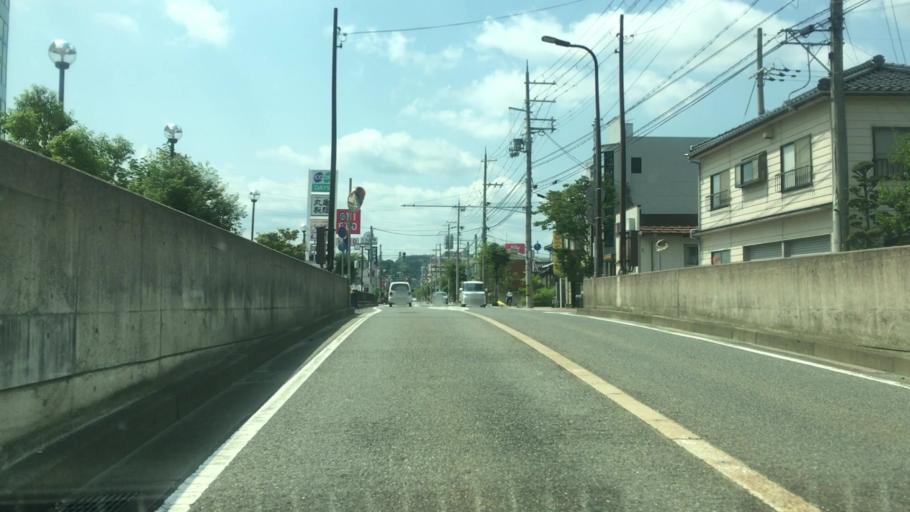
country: JP
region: Hyogo
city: Toyooka
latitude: 35.5509
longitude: 134.8155
